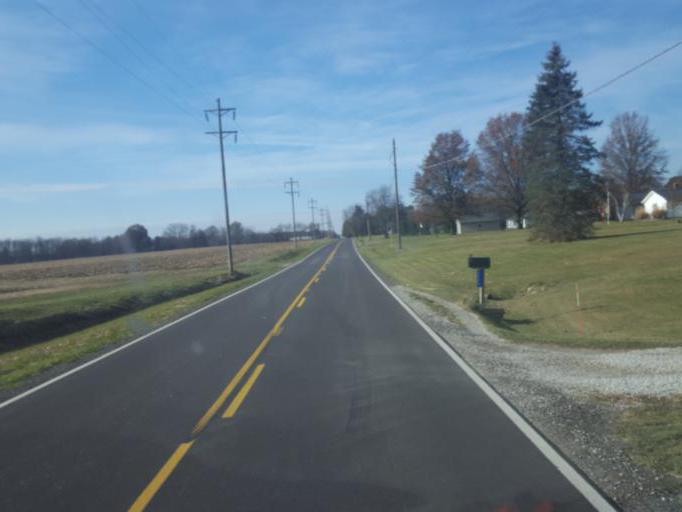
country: US
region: Ohio
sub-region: Crawford County
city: Bucyrus
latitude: 40.8345
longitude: -82.8677
